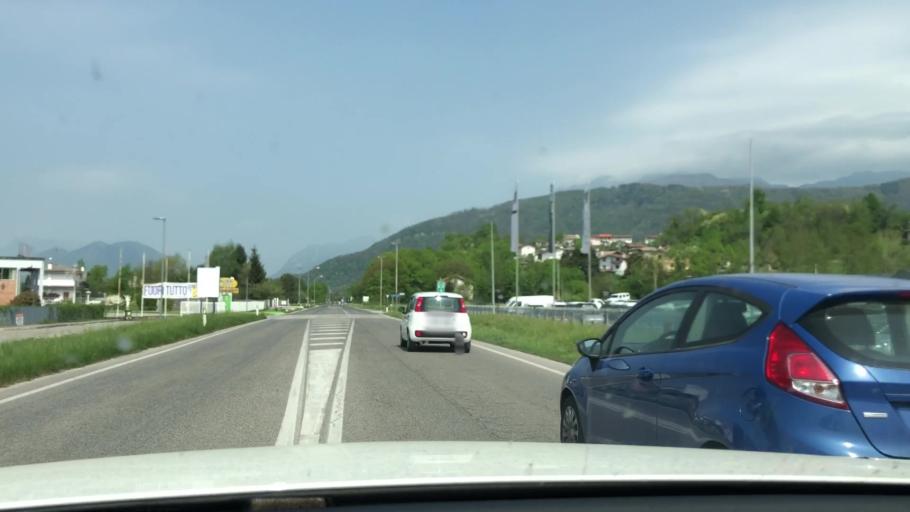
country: IT
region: Friuli Venezia Giulia
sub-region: Provincia di Udine
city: Magnano in Riviera
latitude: 46.2079
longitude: 13.1869
